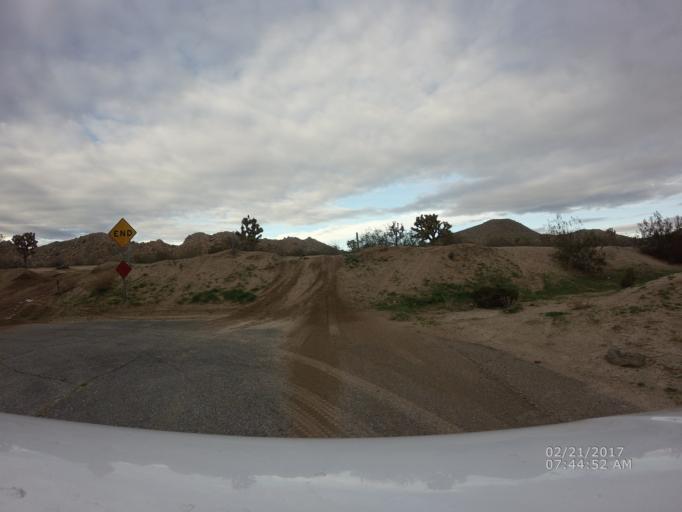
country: US
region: California
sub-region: Los Angeles County
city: Lake Los Angeles
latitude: 34.5971
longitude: -117.8443
